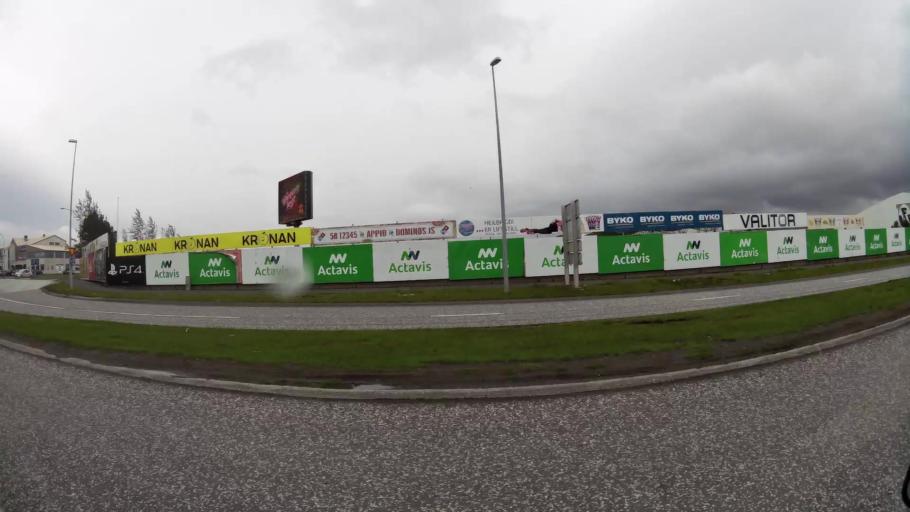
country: IS
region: Capital Region
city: Hafnarfjoerdur
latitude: 64.0756
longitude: -21.9404
